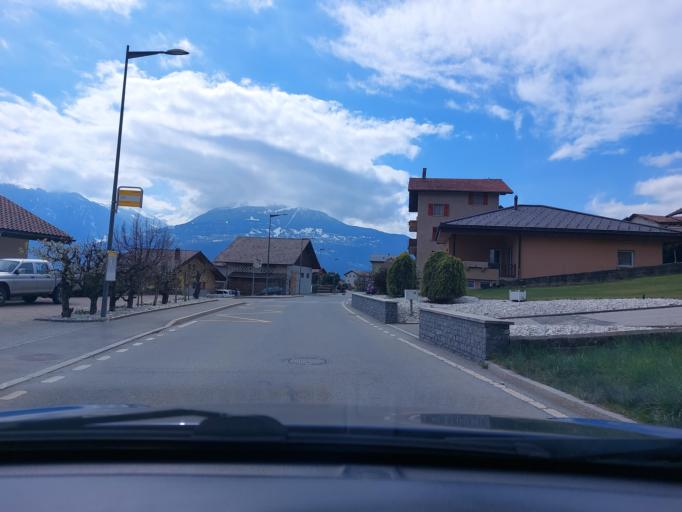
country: CH
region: Valais
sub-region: Conthey District
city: Conthey
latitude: 46.2434
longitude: 7.2963
